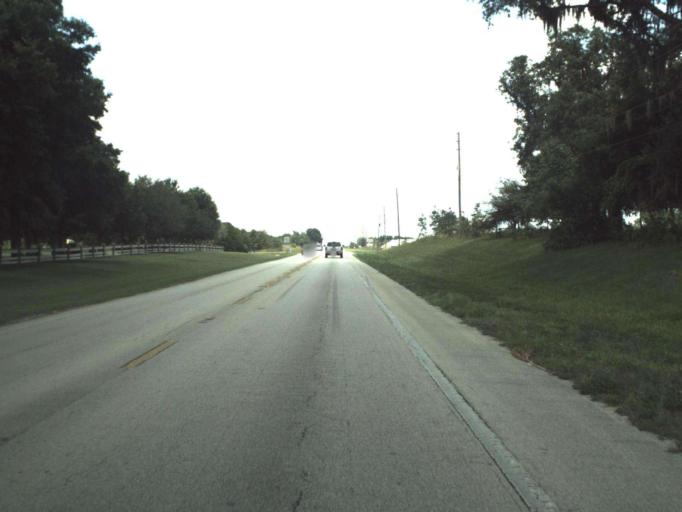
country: US
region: Florida
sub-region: Marion County
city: Silver Springs Shores
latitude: 29.0916
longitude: -82.0535
